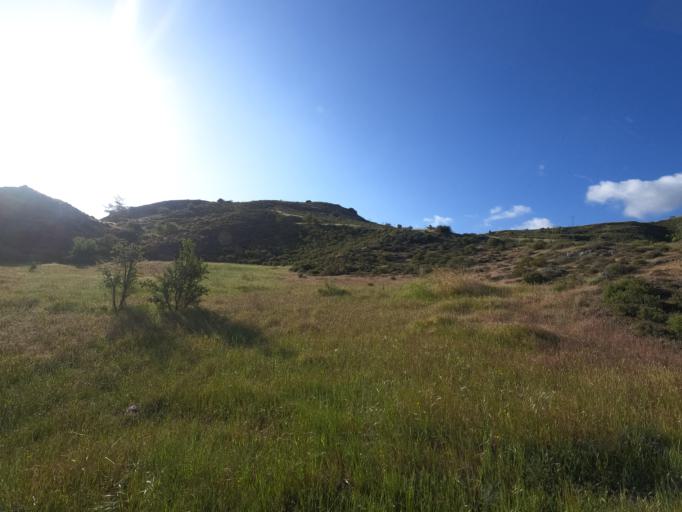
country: CY
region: Lefkosia
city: Astromeritis
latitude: 35.0744
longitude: 33.0395
